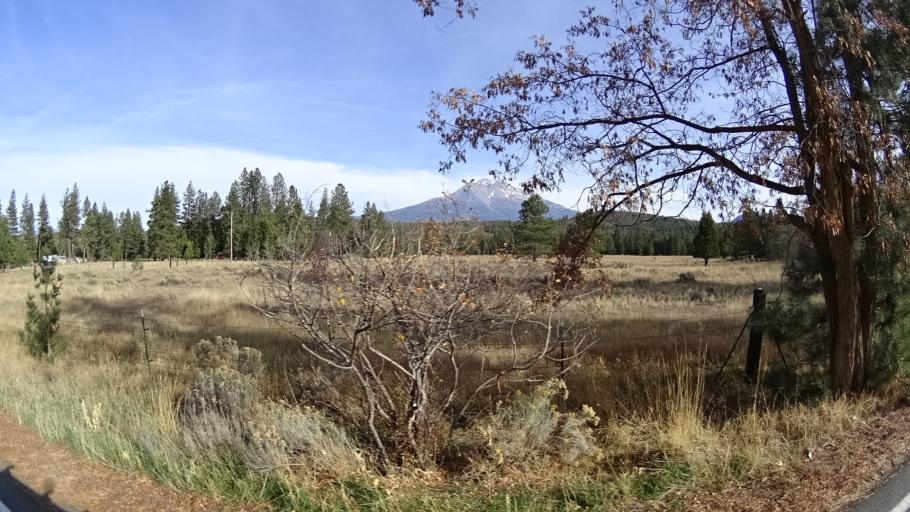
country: US
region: California
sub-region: Siskiyou County
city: Weed
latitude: 41.4153
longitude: -122.4342
